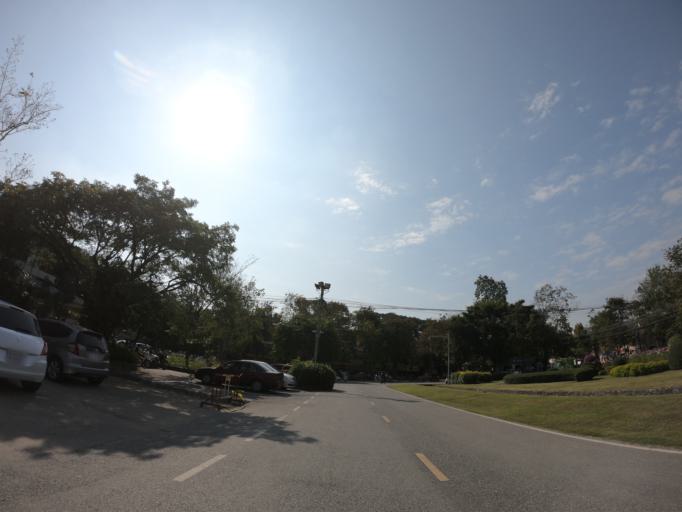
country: TH
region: Chiang Mai
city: Chiang Mai
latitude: 18.7939
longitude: 98.9593
